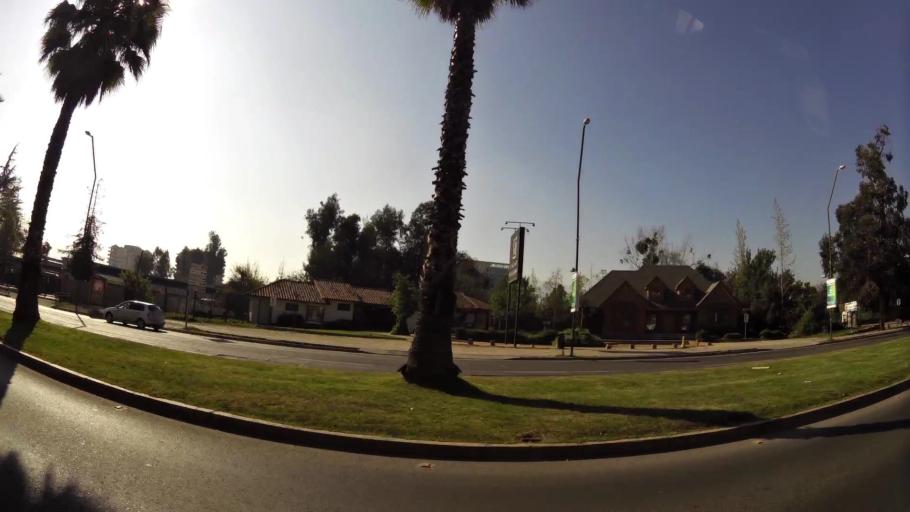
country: CL
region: Santiago Metropolitan
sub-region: Provincia de Santiago
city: Villa Presidente Frei, Nunoa, Santiago, Chile
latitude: -33.3706
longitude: -70.5102
